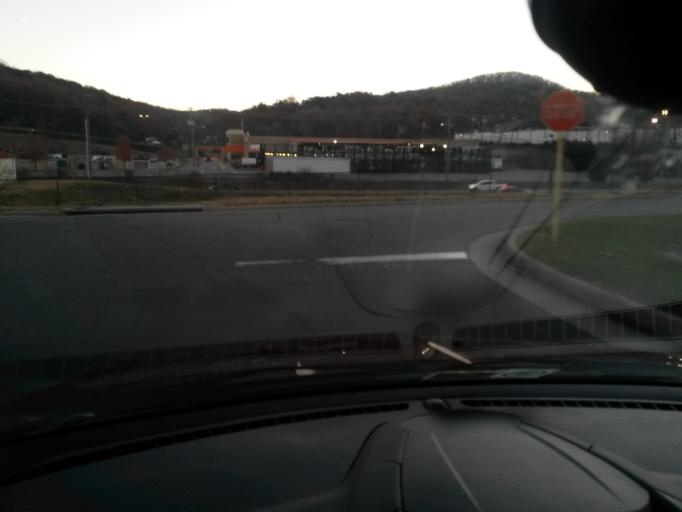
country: US
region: Virginia
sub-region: Roanoke County
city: Narrows
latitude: 37.2245
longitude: -79.9698
